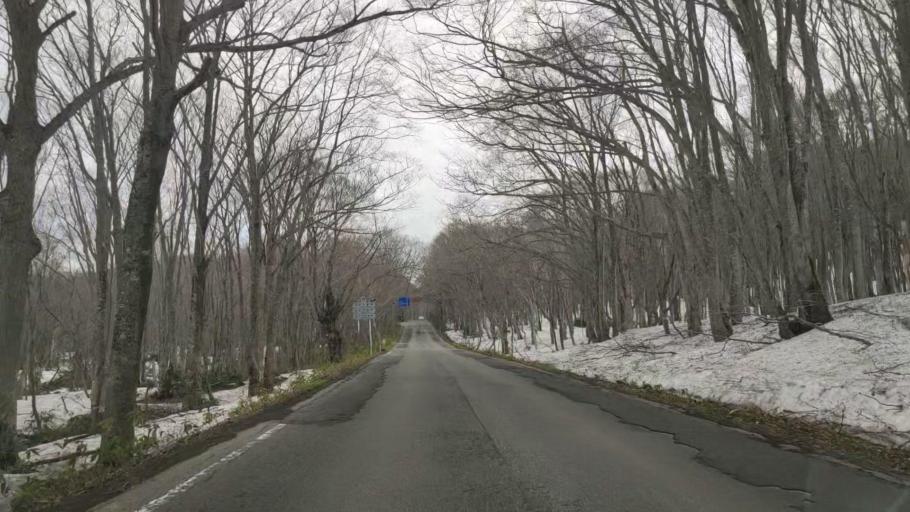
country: JP
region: Aomori
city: Aomori Shi
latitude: 40.6979
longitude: 140.9036
